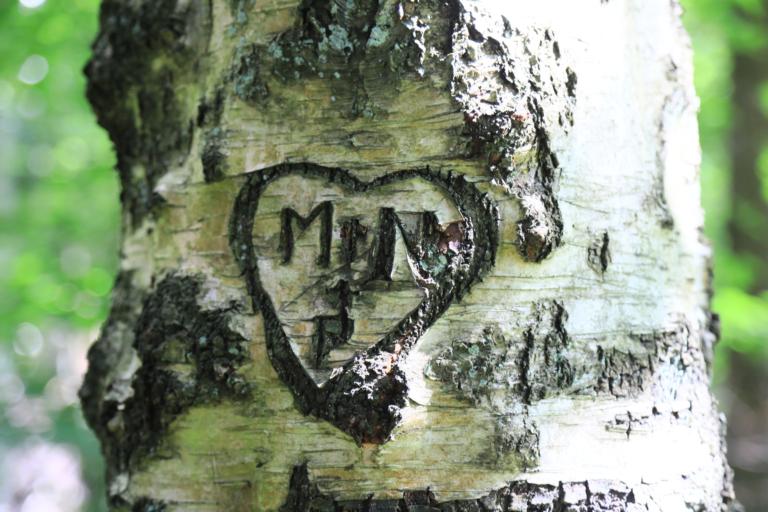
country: SE
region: Halland
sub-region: Varbergs Kommun
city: Varberg
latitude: 57.1194
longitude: 12.2672
